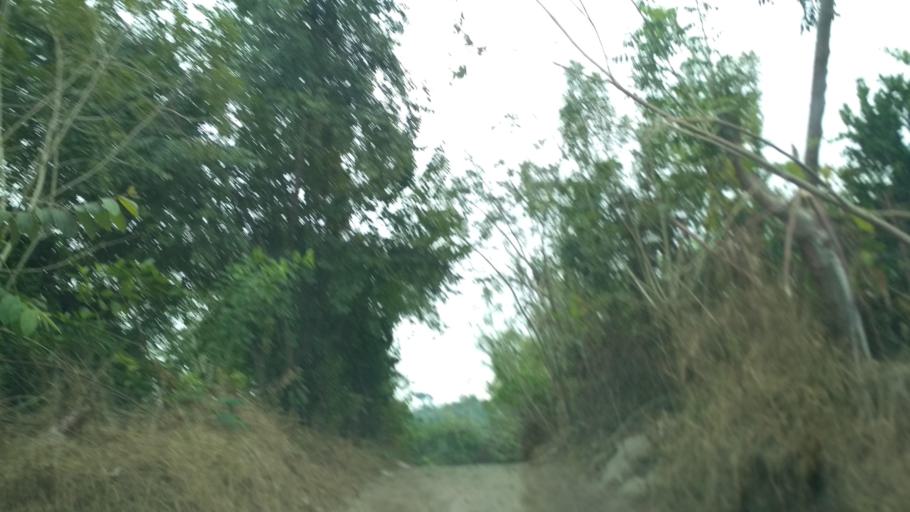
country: MM
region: Kayah
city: Loikaw
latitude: 20.2123
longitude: 97.3322
